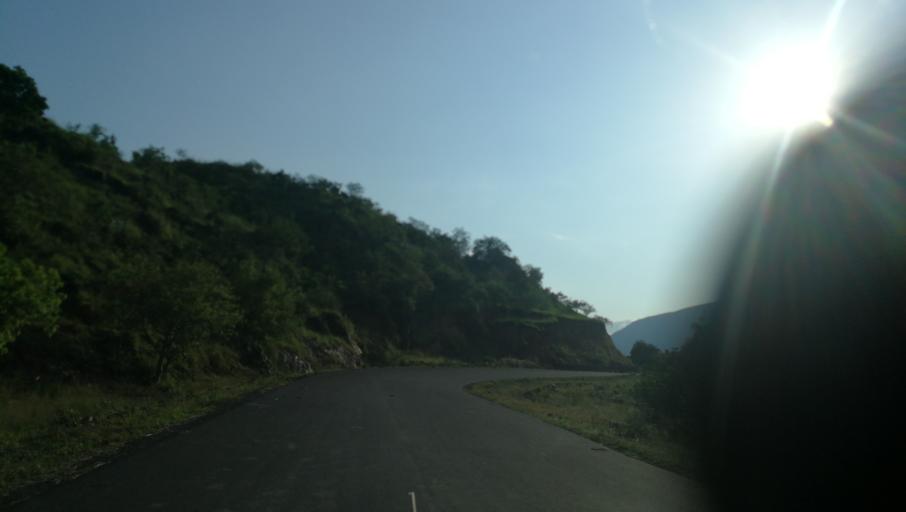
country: ET
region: Southern Nations, Nationalities, and People's Region
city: Areka
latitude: 6.8309
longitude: 37.3101
